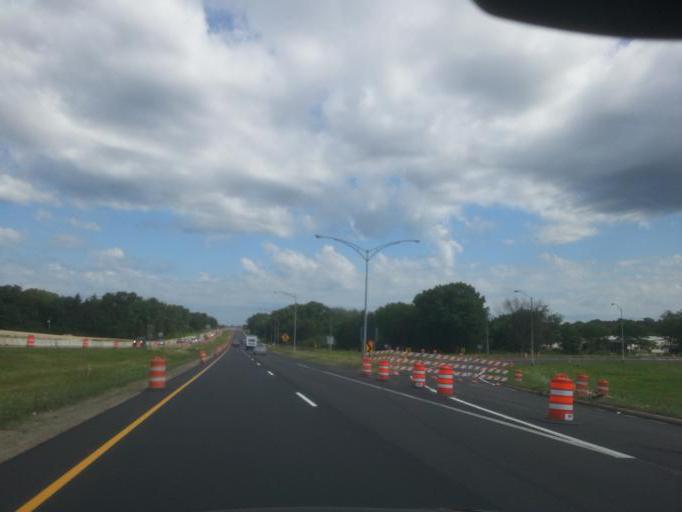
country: US
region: Wisconsin
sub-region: Dane County
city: Monona
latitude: 43.0849
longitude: -89.3115
